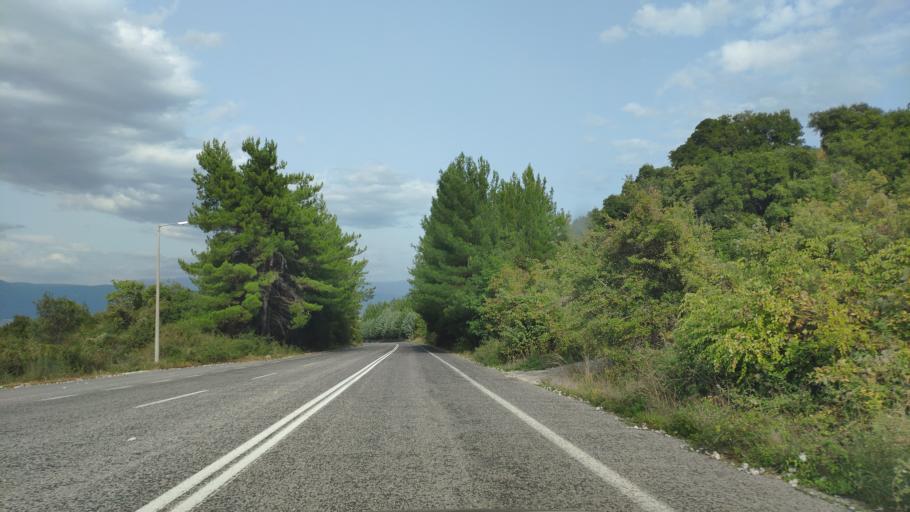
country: GR
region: Central Greece
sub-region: Nomos Fthiotidos
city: Anthili
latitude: 38.7956
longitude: 22.4855
